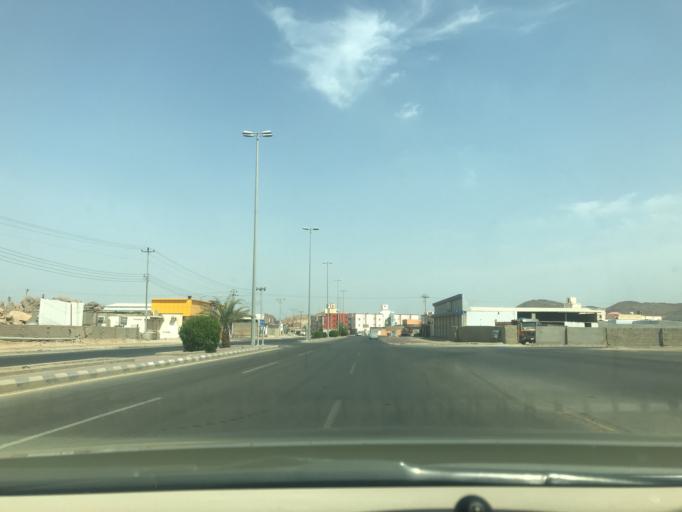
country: SA
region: Makkah
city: Al Jumum
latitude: 21.6263
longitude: 39.6677
